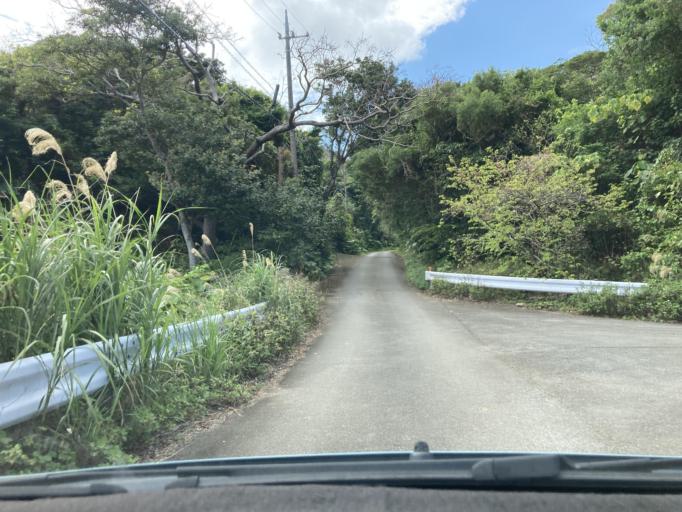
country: JP
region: Okinawa
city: Nago
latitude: 26.6900
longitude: 127.9274
